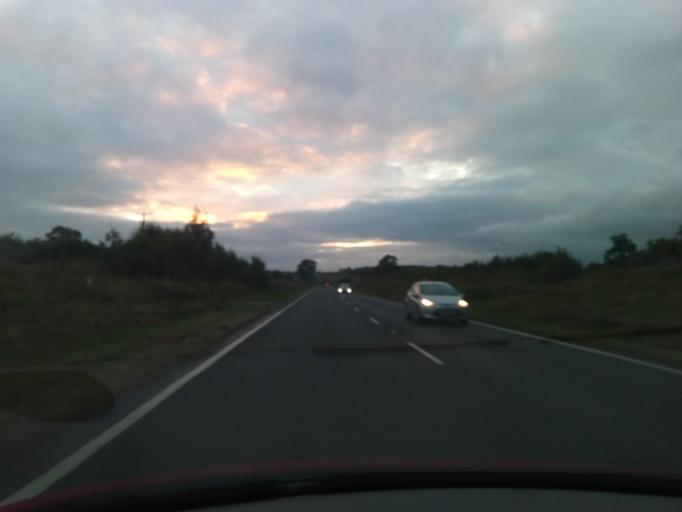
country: GB
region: England
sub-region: County Durham
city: High Etherley
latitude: 54.6257
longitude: -1.7181
